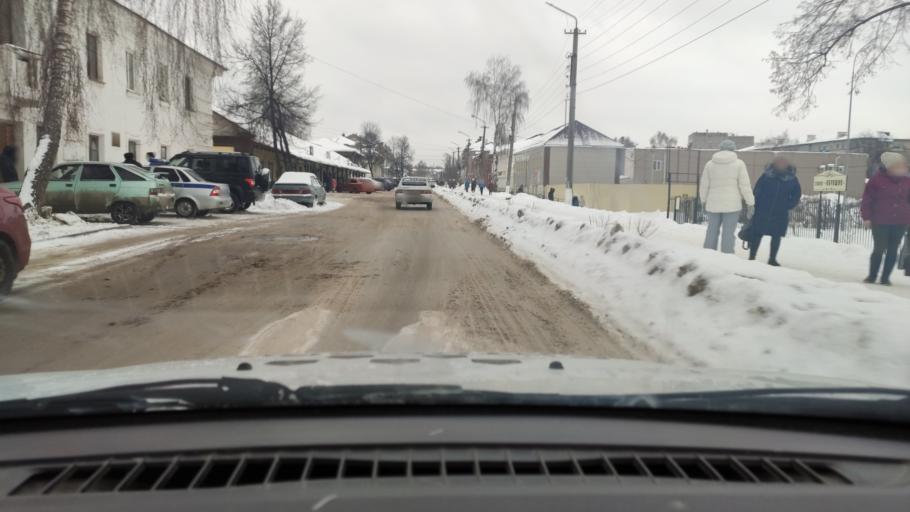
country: RU
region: Perm
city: Kungur
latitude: 57.4389
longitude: 56.9348
